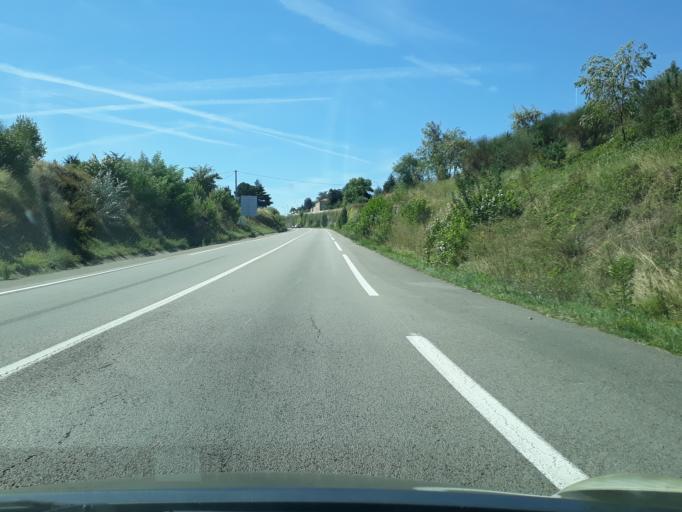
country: FR
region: Rhone-Alpes
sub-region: Departement de l'Ardeche
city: Peaugres
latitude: 45.2817
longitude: 4.7251
